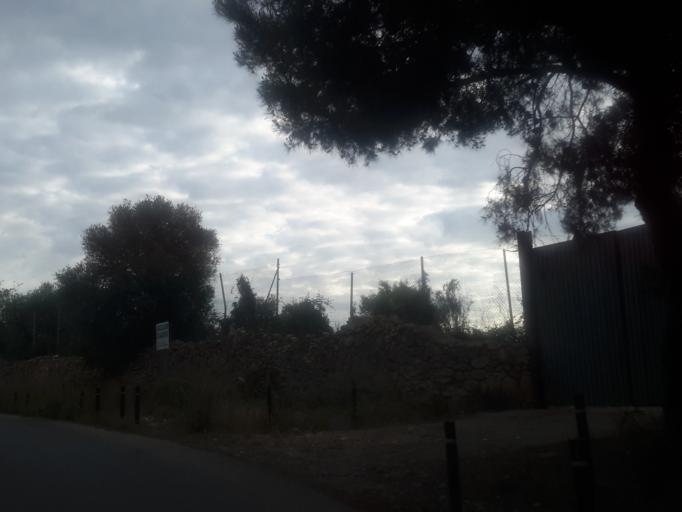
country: ES
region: Catalonia
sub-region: Provincia de Barcelona
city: Vilanova i la Geltru
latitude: 41.2348
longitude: 1.7041
